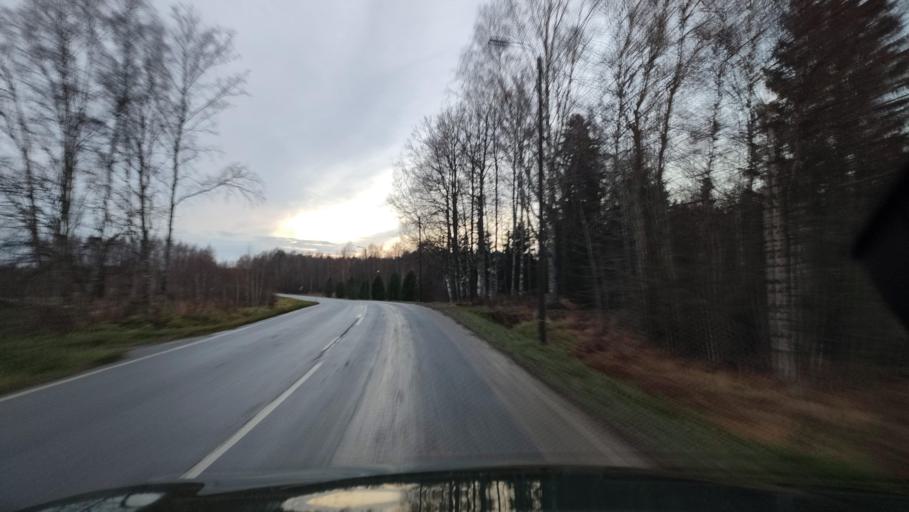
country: FI
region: Ostrobothnia
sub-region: Vaasa
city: Ristinummi
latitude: 63.0480
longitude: 21.7397
